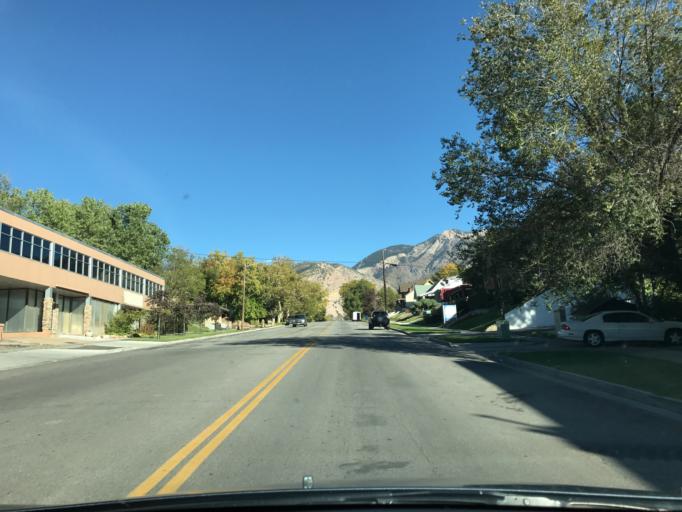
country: US
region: Utah
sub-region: Weber County
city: Ogden
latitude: 41.2185
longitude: -111.9675
